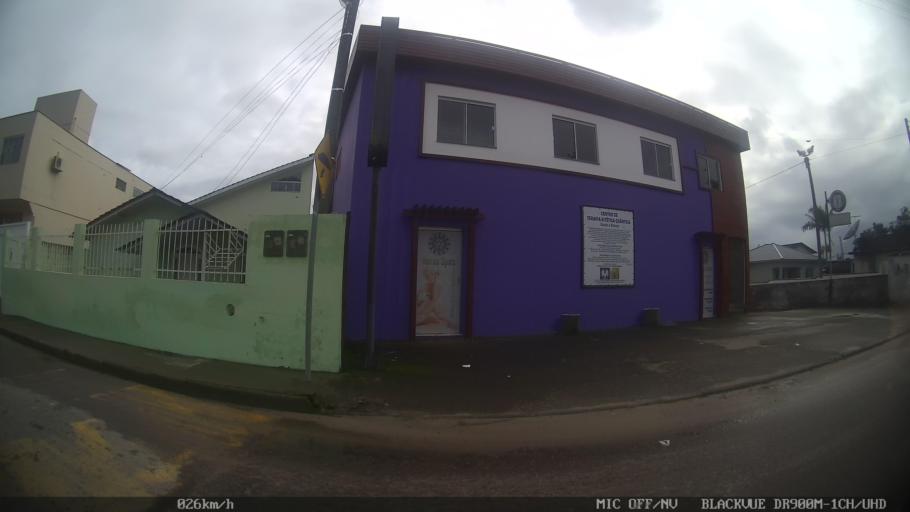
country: BR
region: Santa Catarina
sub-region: Biguacu
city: Biguacu
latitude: -27.5171
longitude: -48.6447
